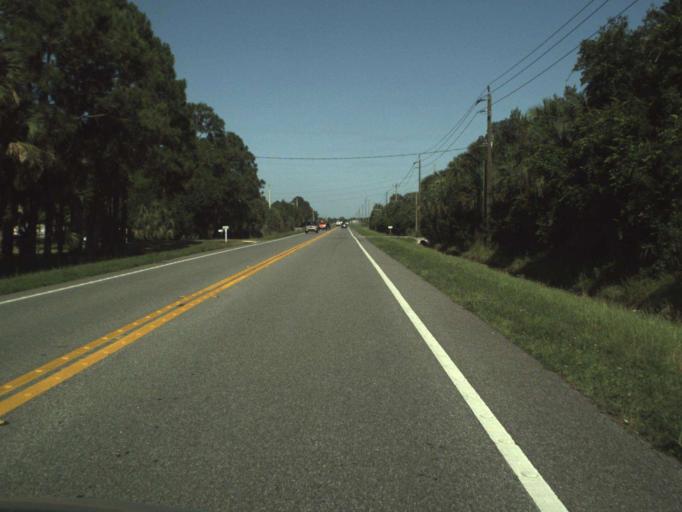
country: US
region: Florida
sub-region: Seminole County
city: Geneva
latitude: 28.7163
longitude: -81.0535
